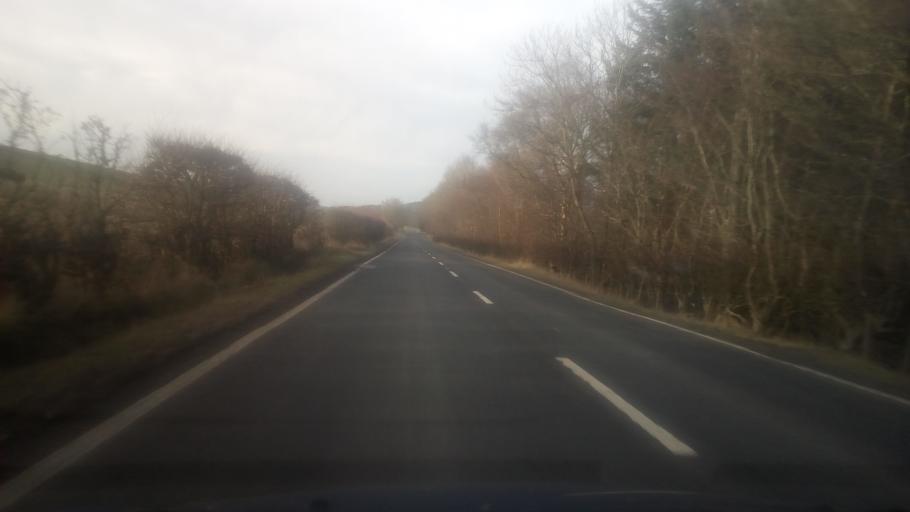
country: GB
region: Scotland
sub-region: The Scottish Borders
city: Jedburgh
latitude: 55.4251
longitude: -2.5298
